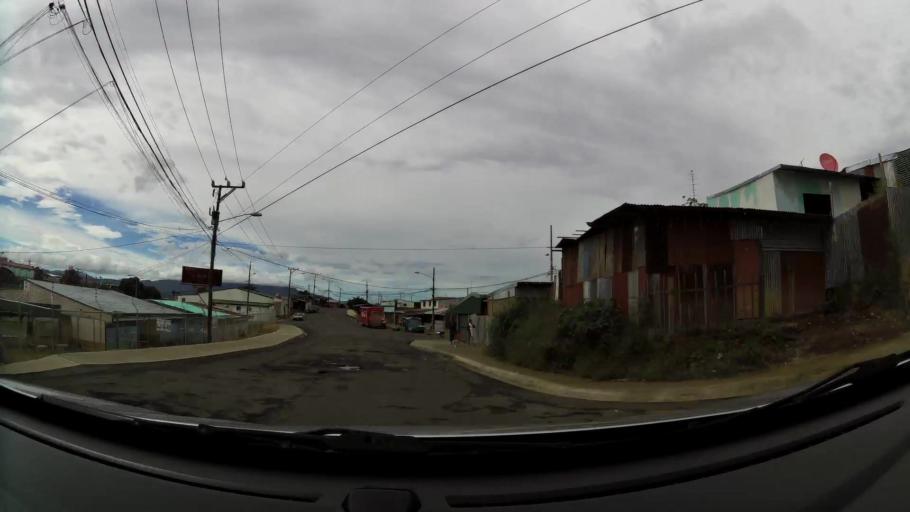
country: CR
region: San Jose
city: Ipis
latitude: 9.9609
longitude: -84.0083
